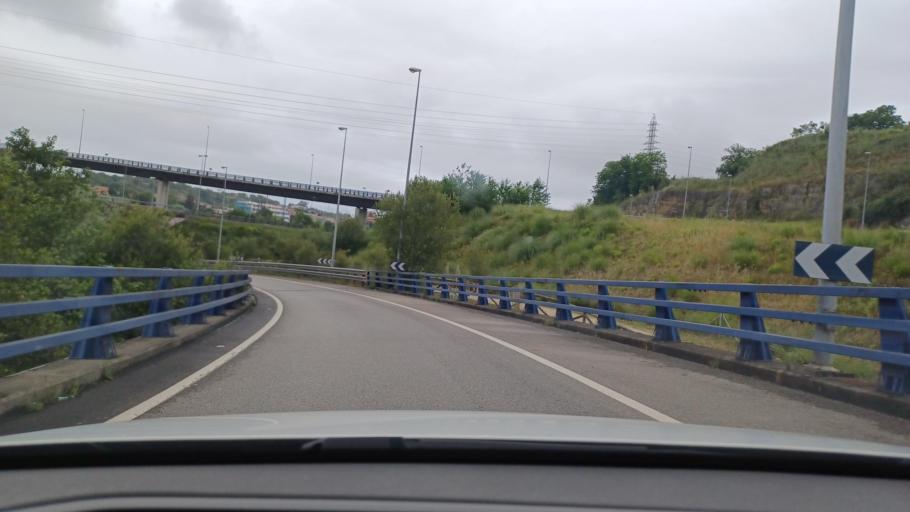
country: ES
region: Asturias
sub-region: Province of Asturias
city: Gijon
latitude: 43.5159
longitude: -5.6549
